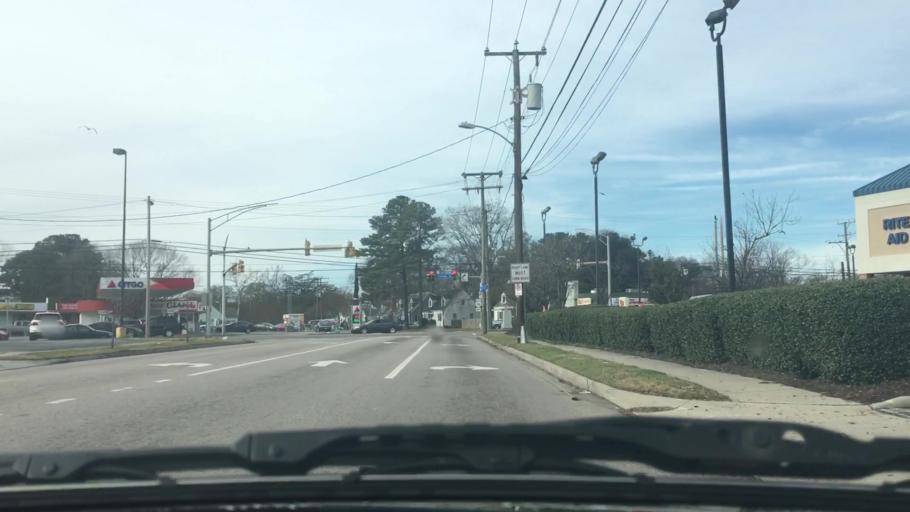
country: US
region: Virginia
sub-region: City of Norfolk
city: Norfolk
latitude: 36.8858
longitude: -76.2596
